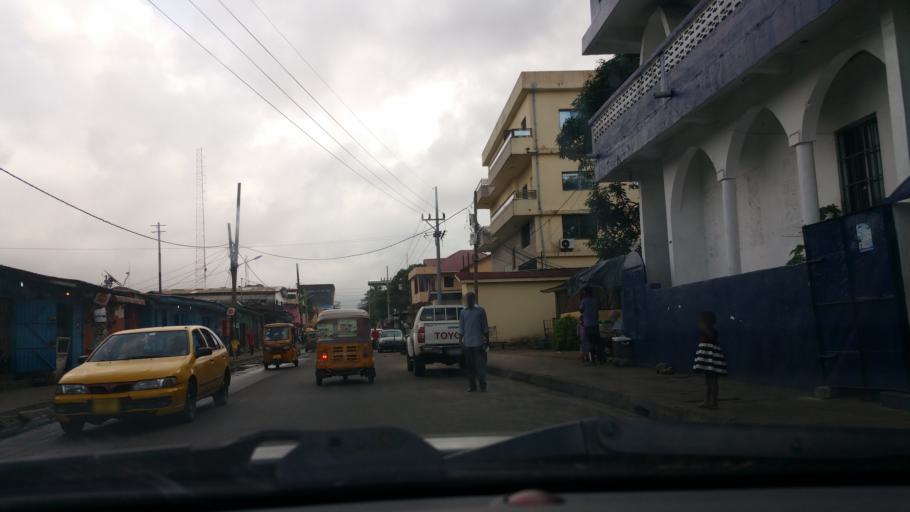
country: LR
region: Montserrado
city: Monrovia
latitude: 6.3129
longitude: -10.8106
